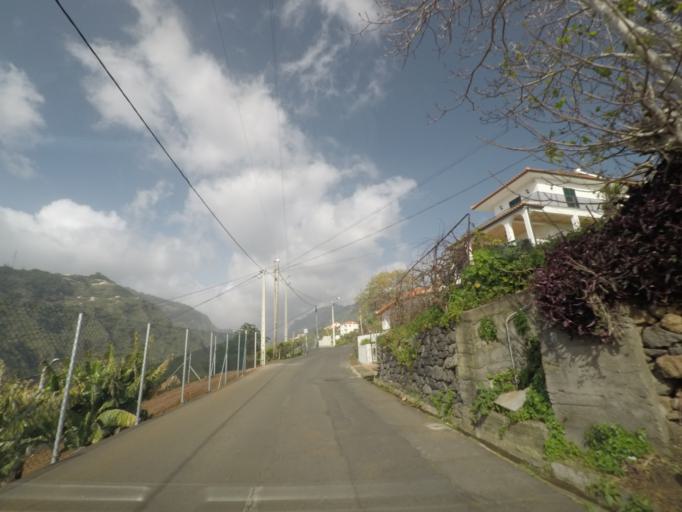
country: PT
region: Madeira
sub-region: Ribeira Brava
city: Campanario
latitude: 32.6742
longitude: -17.0589
